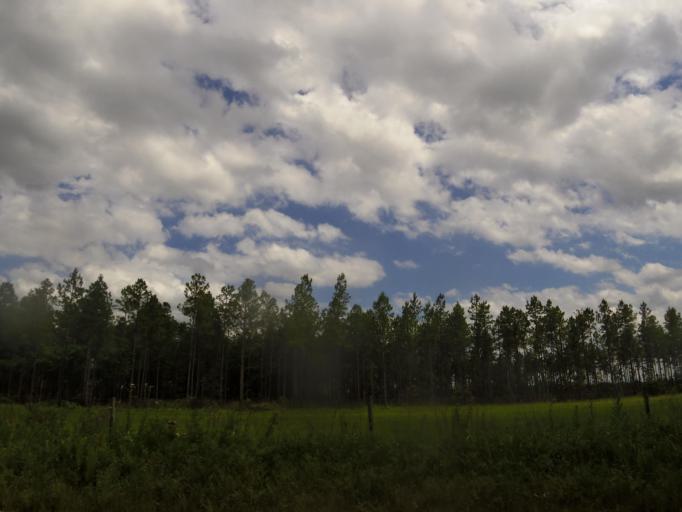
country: US
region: Florida
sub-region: Clay County
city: Asbury Lake
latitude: 29.9033
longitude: -81.8189
